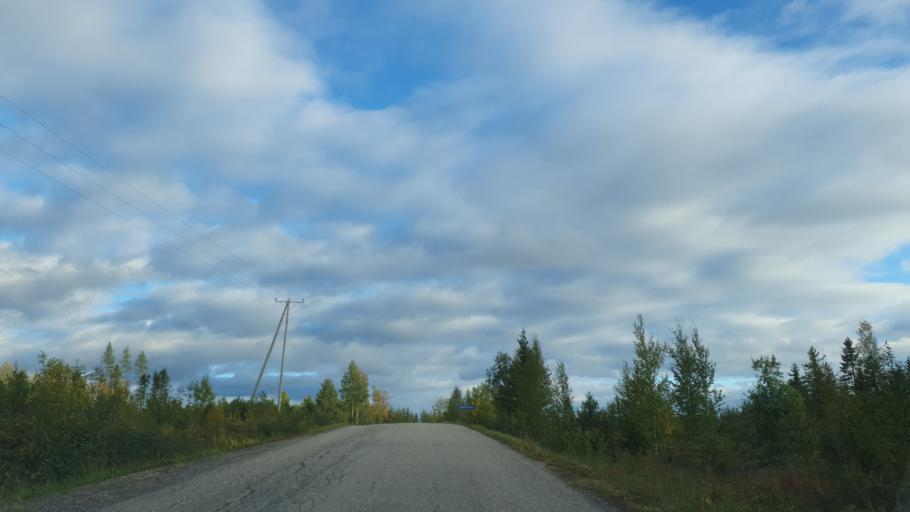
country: FI
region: Kainuu
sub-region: Kehys-Kainuu
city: Kuhmo
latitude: 63.9167
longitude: 30.0711
